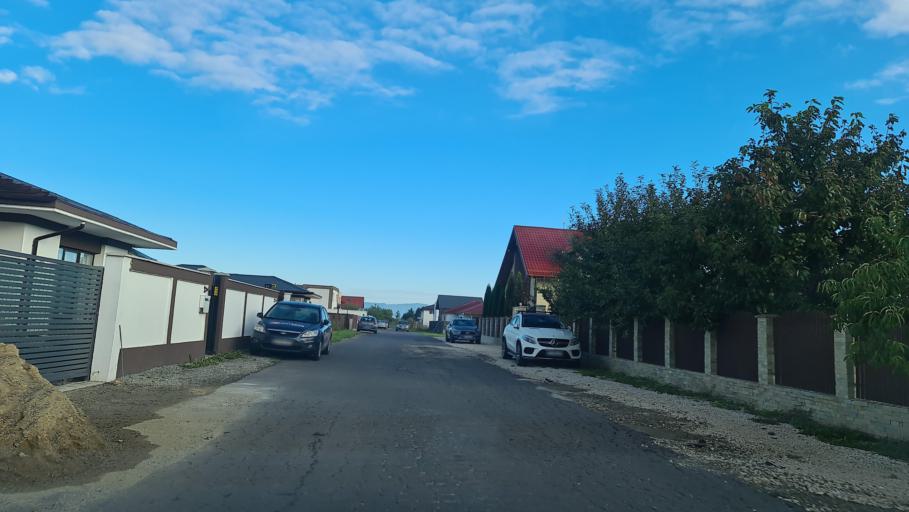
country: RO
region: Brasov
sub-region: Comuna Ghimbav
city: Ghimbav
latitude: 45.6989
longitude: 25.5479
